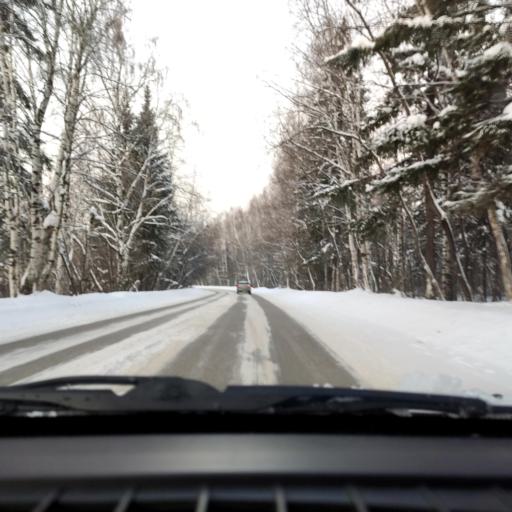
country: RU
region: Perm
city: Overyata
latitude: 58.0523
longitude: 55.8842
